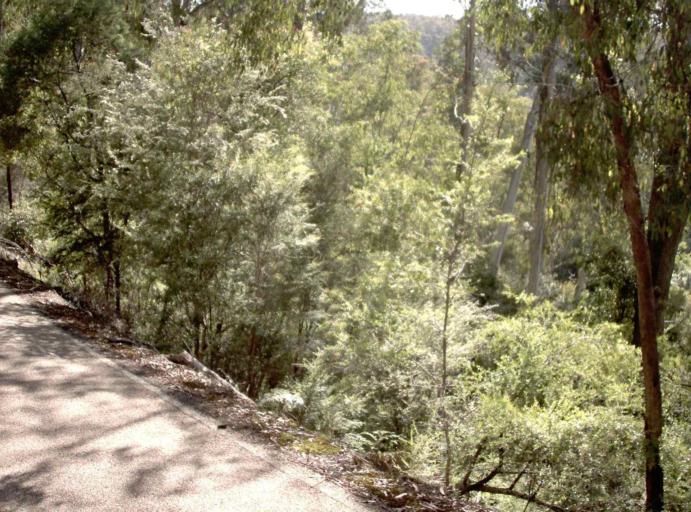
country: AU
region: Victoria
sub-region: East Gippsland
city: Lakes Entrance
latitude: -37.4969
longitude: 148.5527
